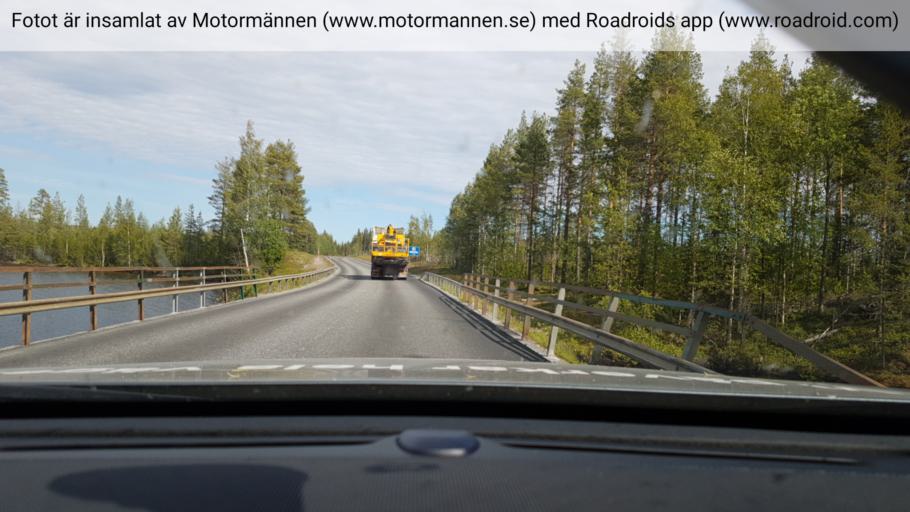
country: SE
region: Vaesterbotten
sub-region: Lycksele Kommun
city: Soderfors
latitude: 64.8309
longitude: 18.0125
